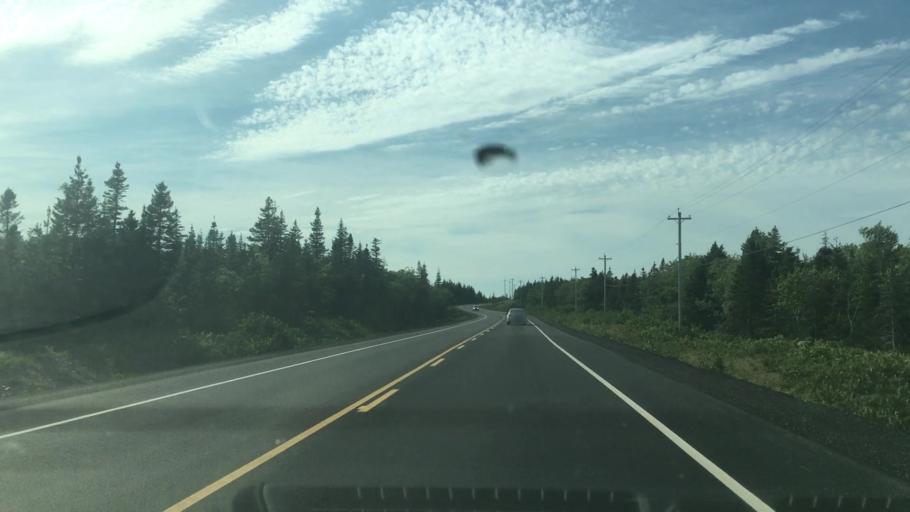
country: CA
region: Nova Scotia
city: Sydney Mines
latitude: 46.8423
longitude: -60.3966
